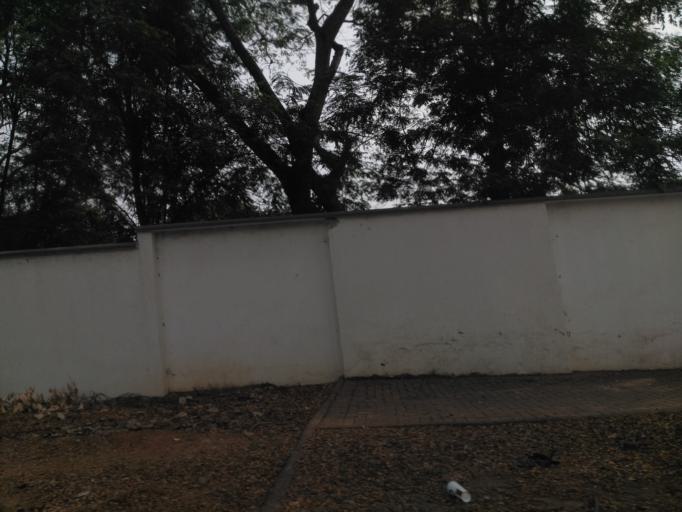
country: GH
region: Ashanti
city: Kumasi
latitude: 6.6830
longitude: -1.6263
